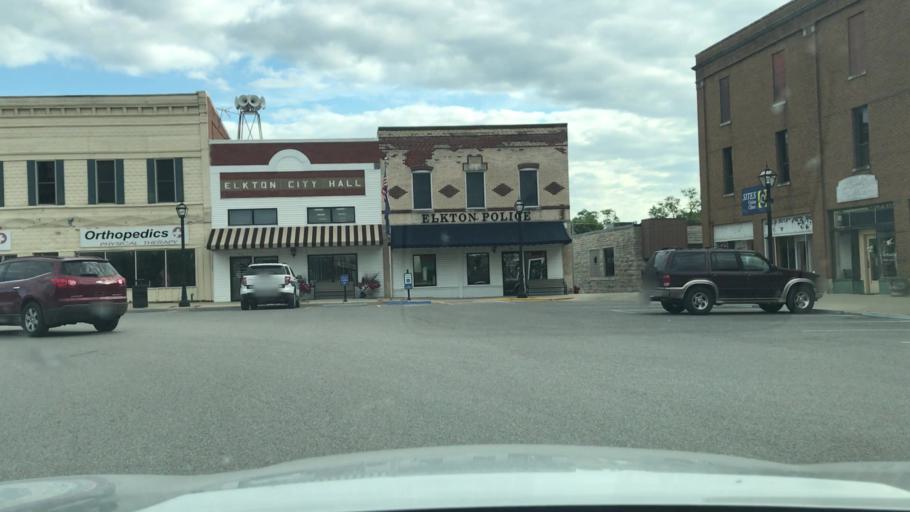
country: US
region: Kentucky
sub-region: Todd County
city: Elkton
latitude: 36.8094
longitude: -87.1537
